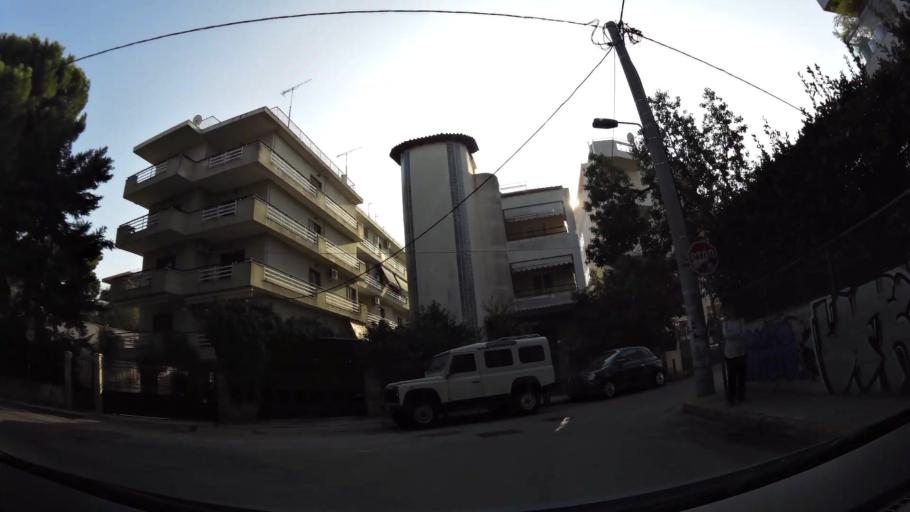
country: GR
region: Attica
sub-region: Nomarchia Athinas
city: Agia Paraskevi
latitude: 38.0097
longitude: 23.8293
